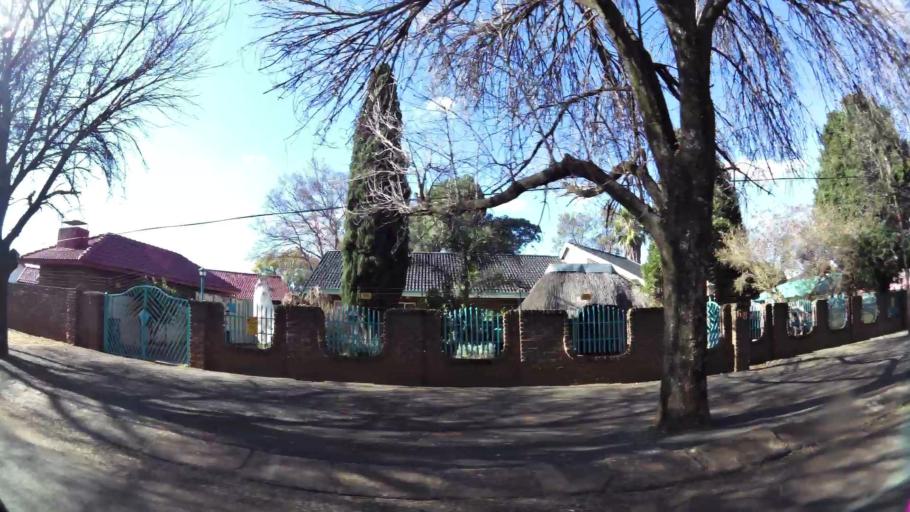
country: ZA
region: Gauteng
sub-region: West Rand District Municipality
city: Carletonville
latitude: -26.3564
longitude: 27.4109
